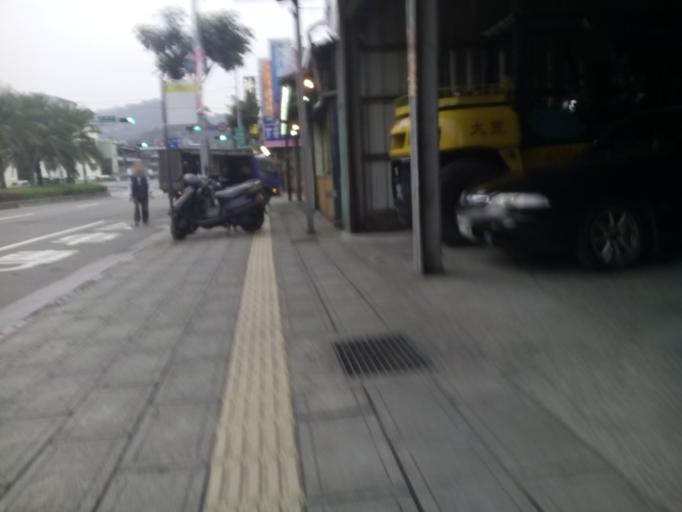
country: TW
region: Taipei
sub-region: Taipei
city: Banqiao
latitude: 24.9832
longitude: 121.4190
